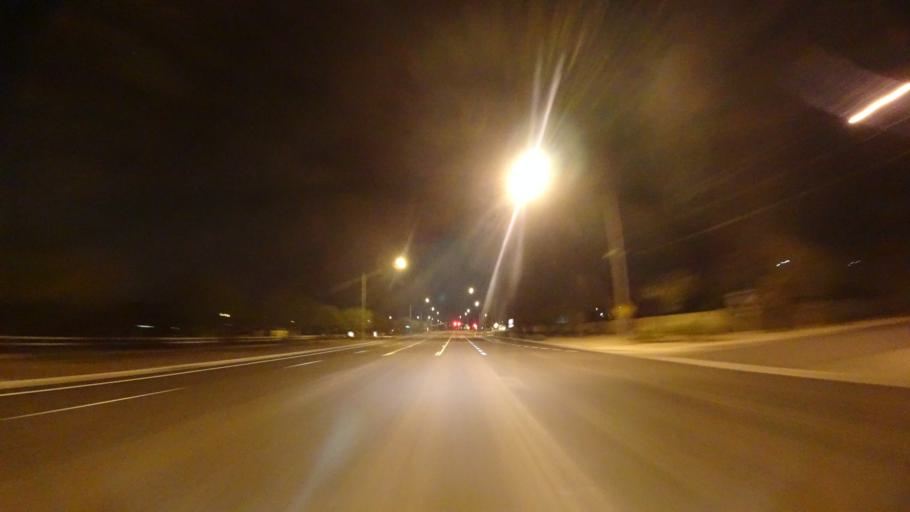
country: US
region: Arizona
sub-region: Maricopa County
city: Gilbert
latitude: 33.3620
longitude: -111.6706
